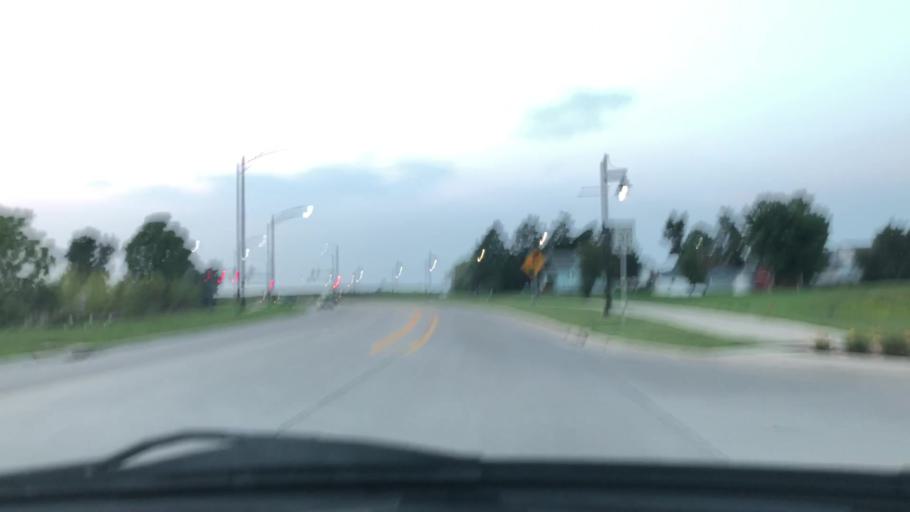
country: US
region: Iowa
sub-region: Johnson County
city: North Liberty
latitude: 41.7581
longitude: -91.6075
